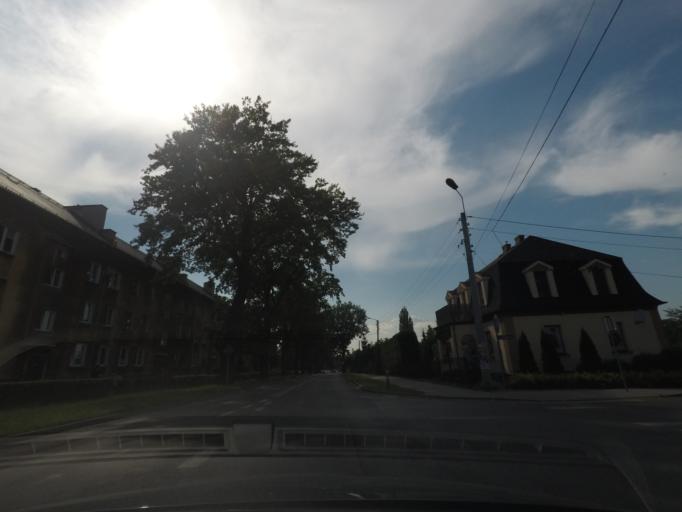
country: PL
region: Lesser Poland Voivodeship
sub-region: Powiat oswiecimski
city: Brzeszcze
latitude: 49.9723
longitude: 19.1334
